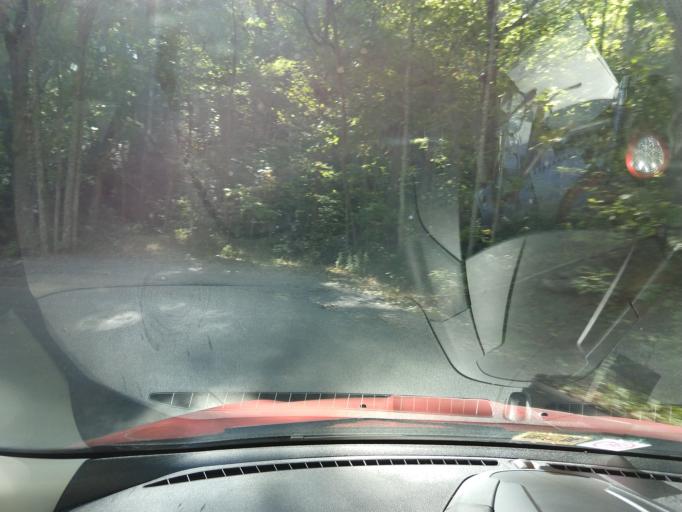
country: US
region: Virginia
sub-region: Alleghany County
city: Clifton Forge
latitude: 37.8602
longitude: -79.8782
